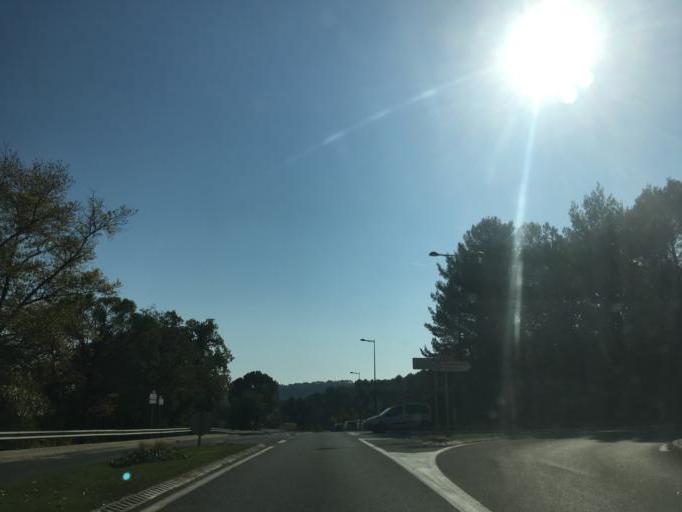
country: FR
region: Provence-Alpes-Cote d'Azur
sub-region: Departement du Var
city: Figanieres
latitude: 43.5662
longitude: 6.5076
